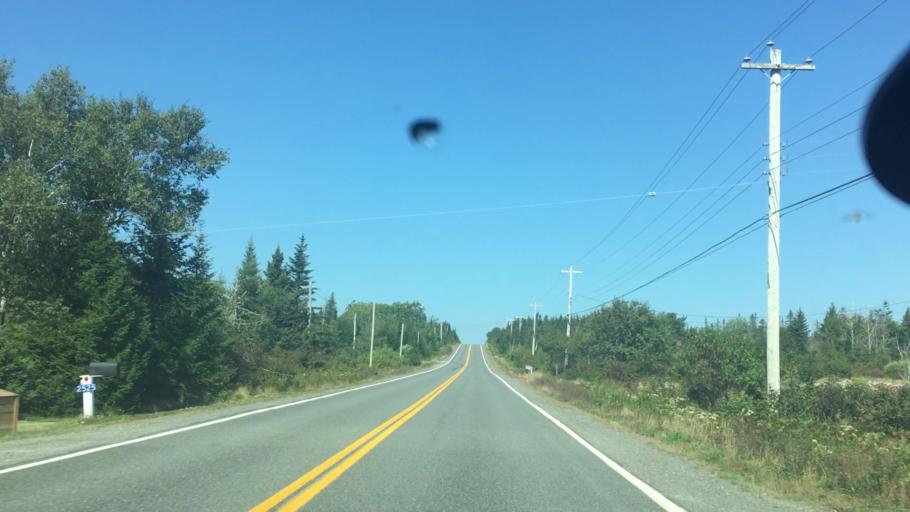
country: CA
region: Nova Scotia
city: Antigonish
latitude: 45.0013
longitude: -62.1003
